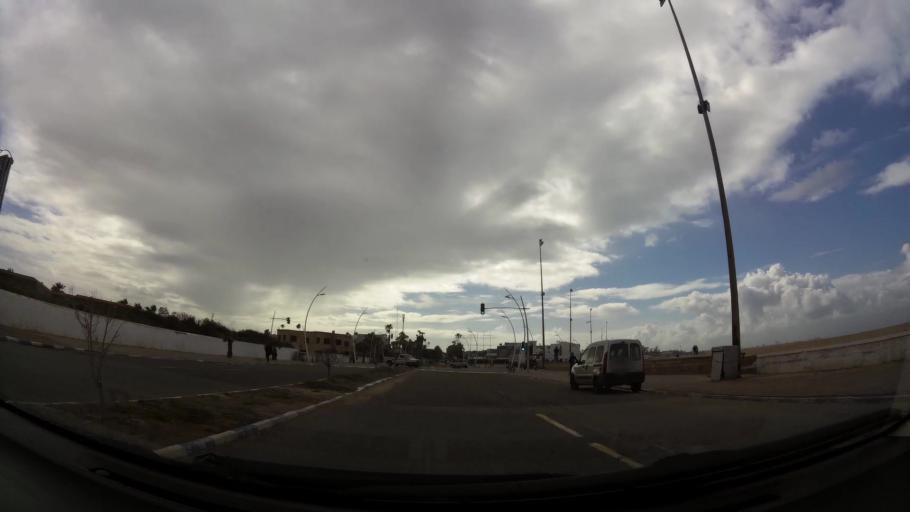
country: MA
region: Doukkala-Abda
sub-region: El-Jadida
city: El Jadida
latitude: 33.2442
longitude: -8.4868
